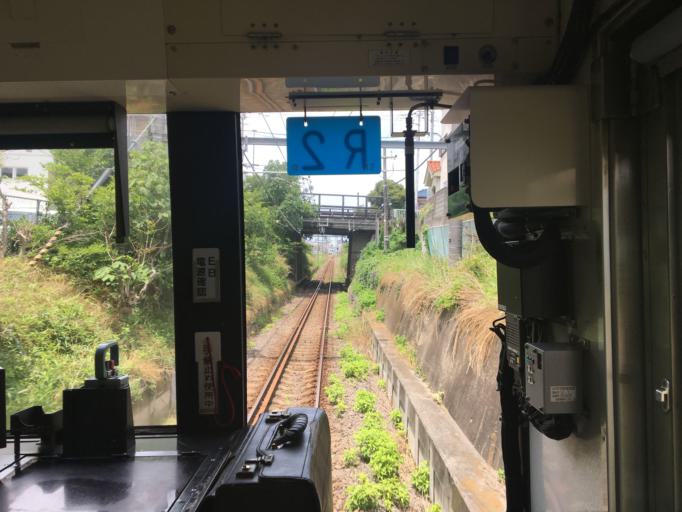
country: JP
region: Kanagawa
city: Chigasaki
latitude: 35.3341
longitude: 139.4106
